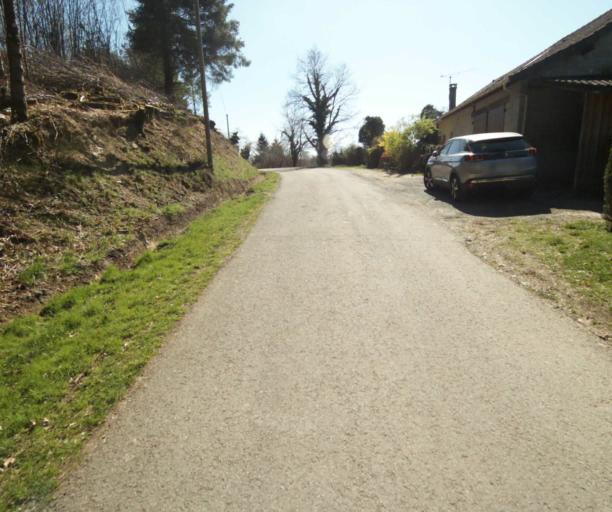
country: FR
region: Limousin
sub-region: Departement de la Correze
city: Saint-Mexant
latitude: 45.3013
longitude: 1.6712
